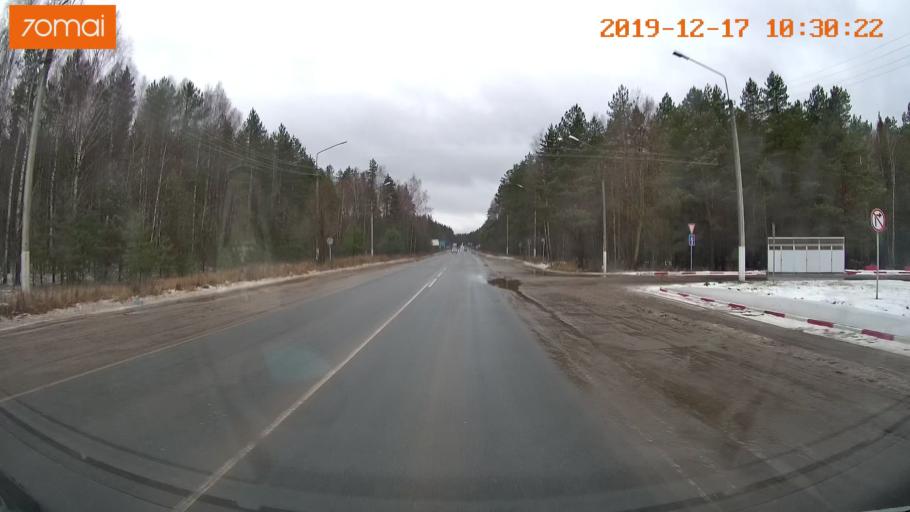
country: RU
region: Vladimir
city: Gus'-Khrustal'nyy
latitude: 55.6433
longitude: 40.7096
